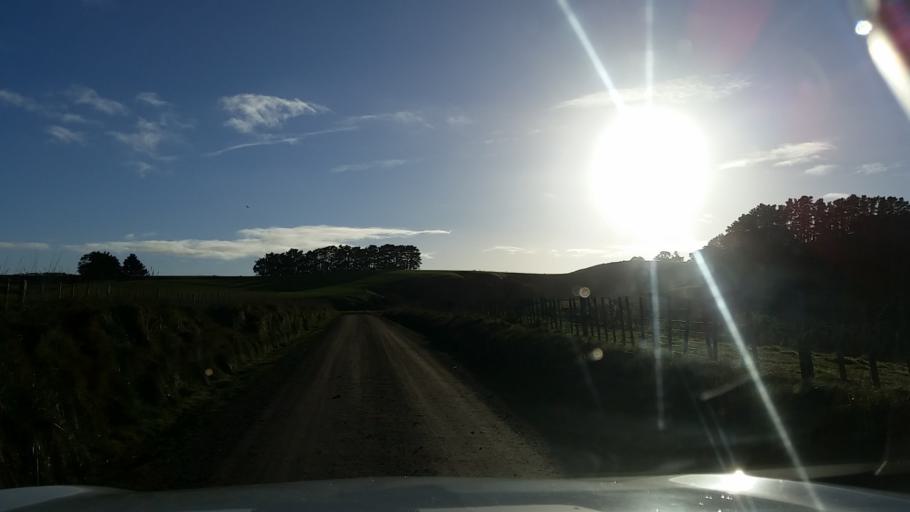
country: NZ
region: Taranaki
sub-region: South Taranaki District
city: Patea
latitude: -39.7571
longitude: 174.7428
